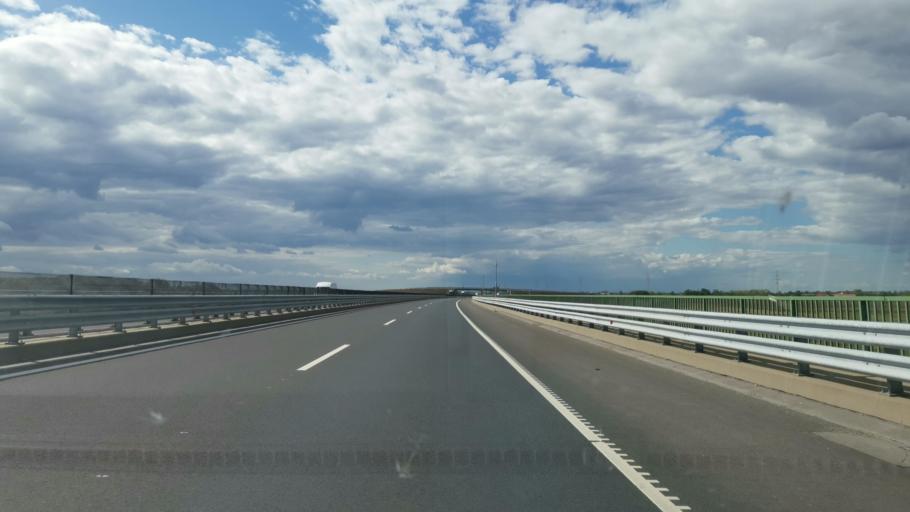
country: HU
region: Jasz-Nagykun-Szolnok
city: Szajol
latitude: 47.2106
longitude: 20.2849
